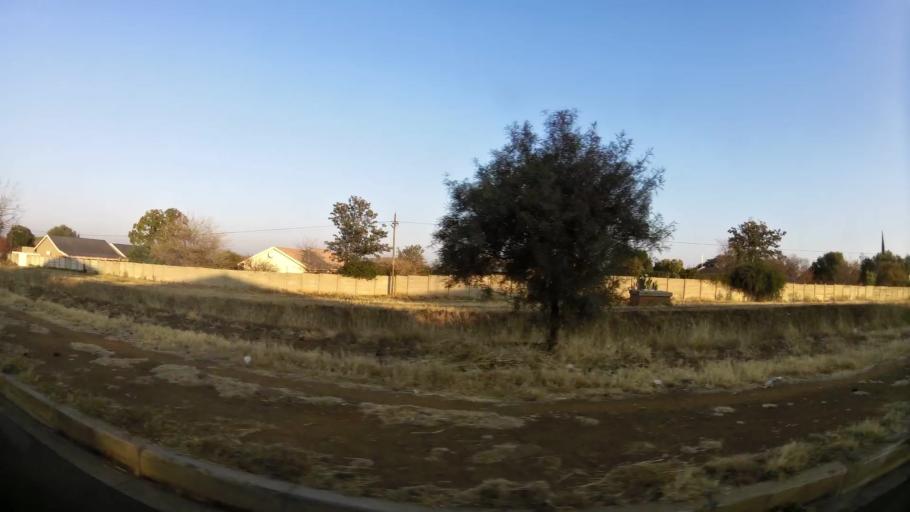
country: ZA
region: Orange Free State
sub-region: Mangaung Metropolitan Municipality
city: Bloemfontein
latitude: -29.0960
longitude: 26.1641
